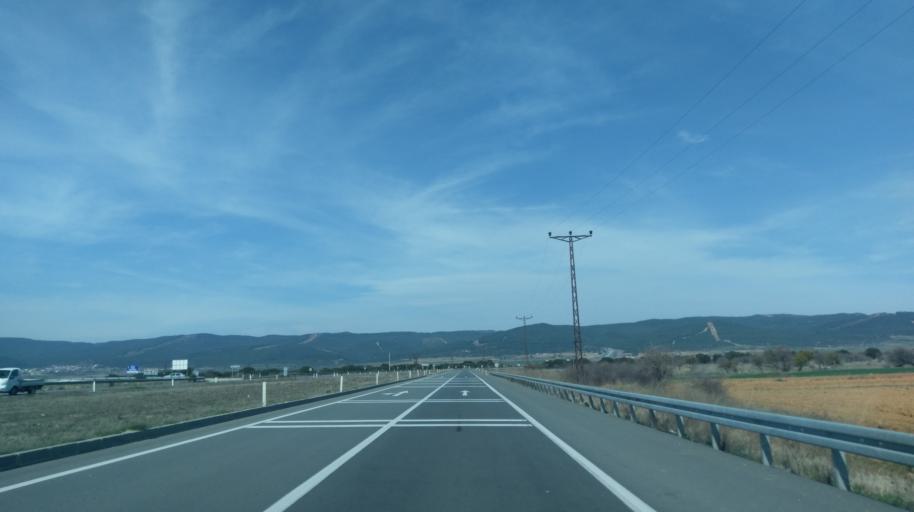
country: TR
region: Canakkale
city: Evrese
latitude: 40.6650
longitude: 26.8062
